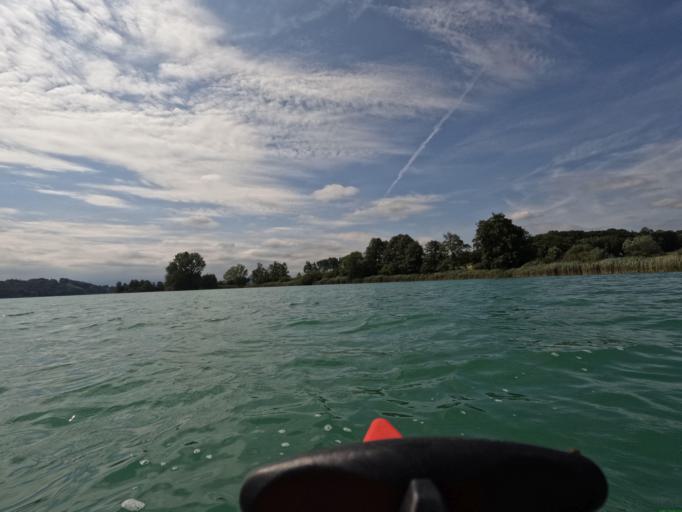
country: DE
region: Bavaria
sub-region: Upper Bavaria
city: Taching am See
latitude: 47.9837
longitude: 12.7397
